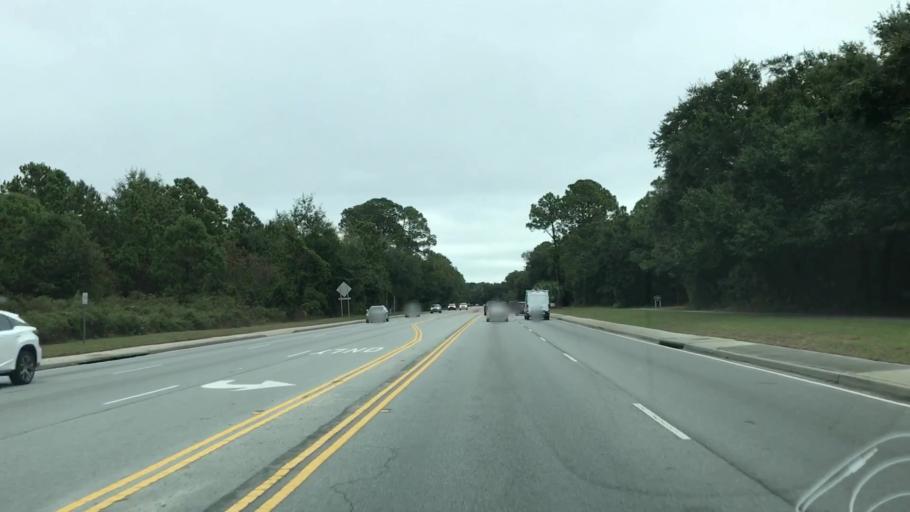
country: US
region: South Carolina
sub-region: Beaufort County
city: Hilton Head Island
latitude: 32.1941
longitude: -80.7057
